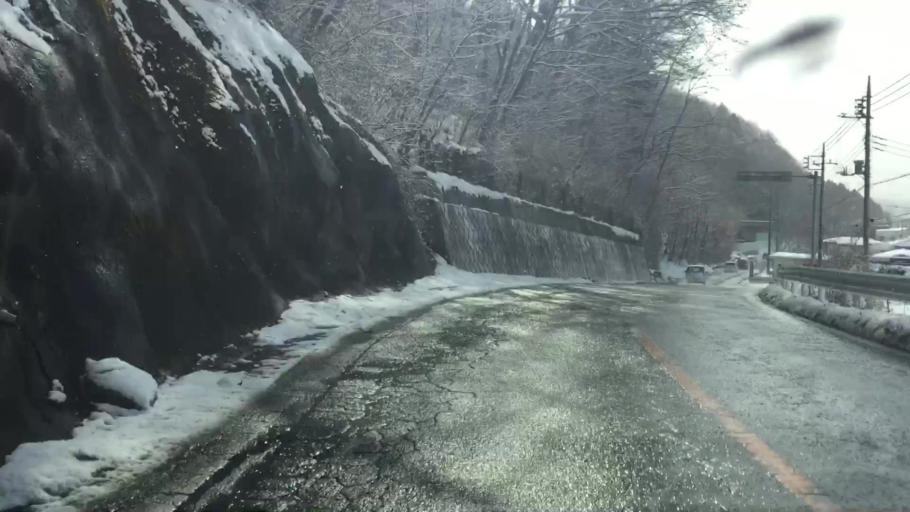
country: JP
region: Gunma
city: Numata
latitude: 36.6792
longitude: 139.0635
